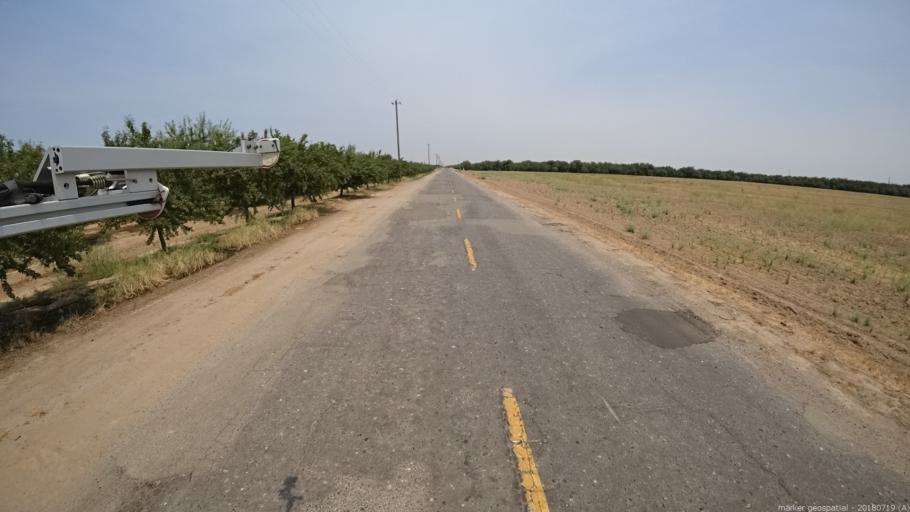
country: US
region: California
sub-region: Madera County
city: Fairmead
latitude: 37.0927
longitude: -120.1840
